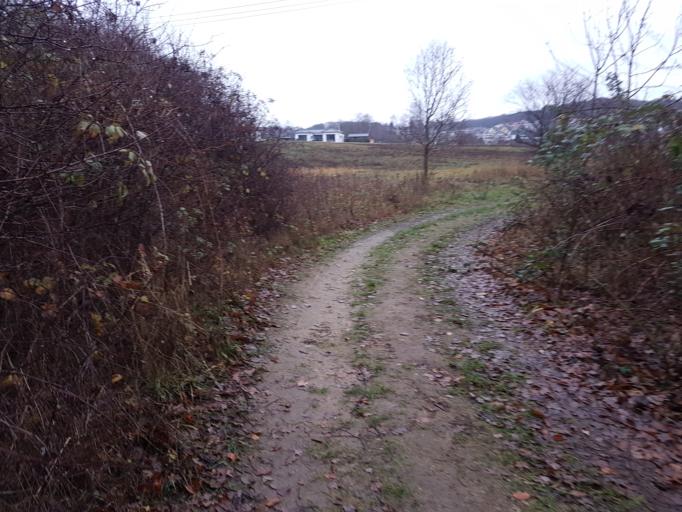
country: DE
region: Mecklenburg-Vorpommern
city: Ostseebad Binz
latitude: 54.3927
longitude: 13.6017
